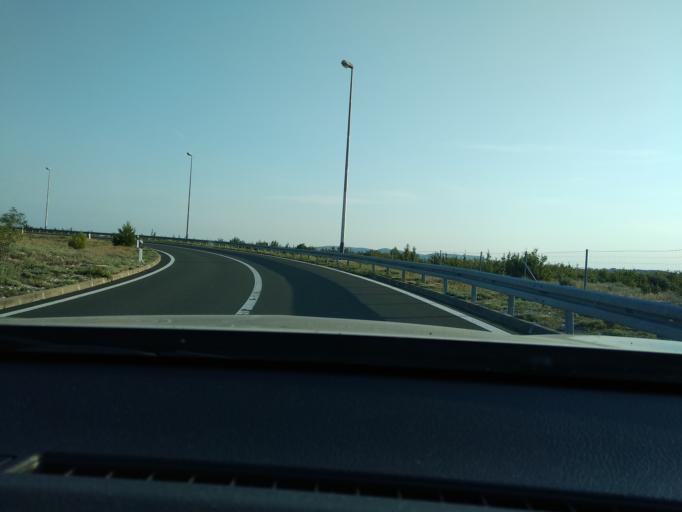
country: HR
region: Sibensko-Kniniska
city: Zaton
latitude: 43.8897
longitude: 15.7906
